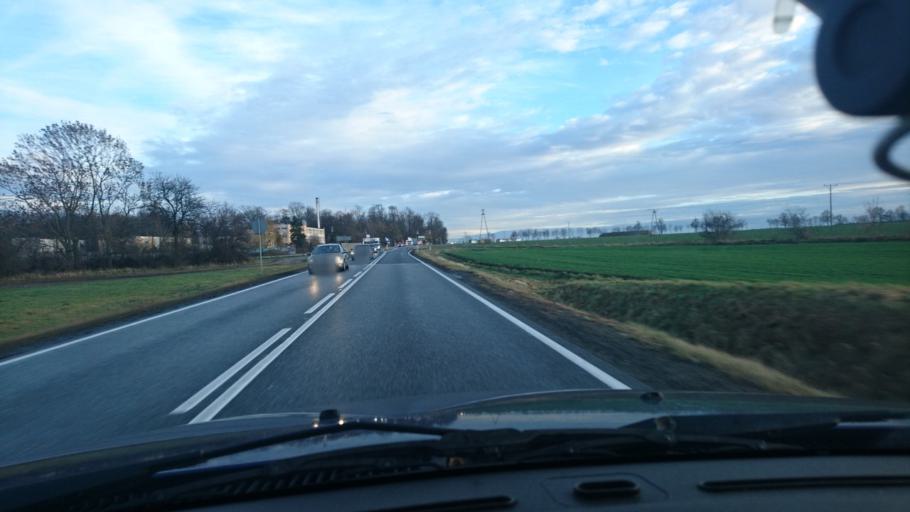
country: PL
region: Greater Poland Voivodeship
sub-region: Powiat kepinski
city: Slupia pod Kepnem
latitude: 51.2424
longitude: 18.0301
